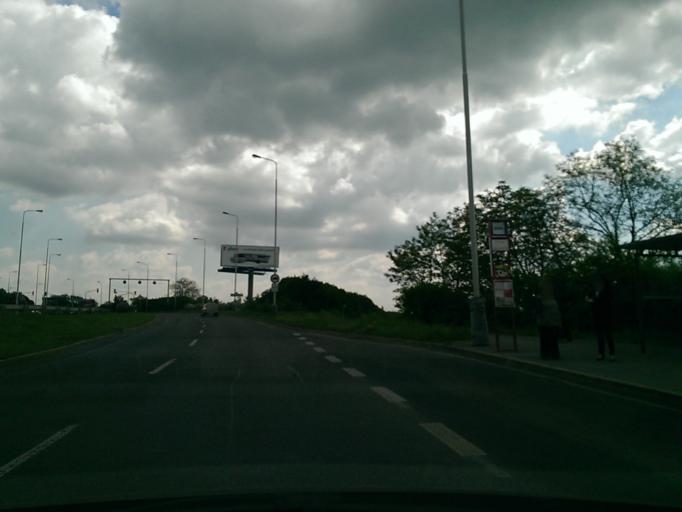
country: CZ
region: Praha
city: Branik
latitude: 50.0463
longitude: 14.3476
